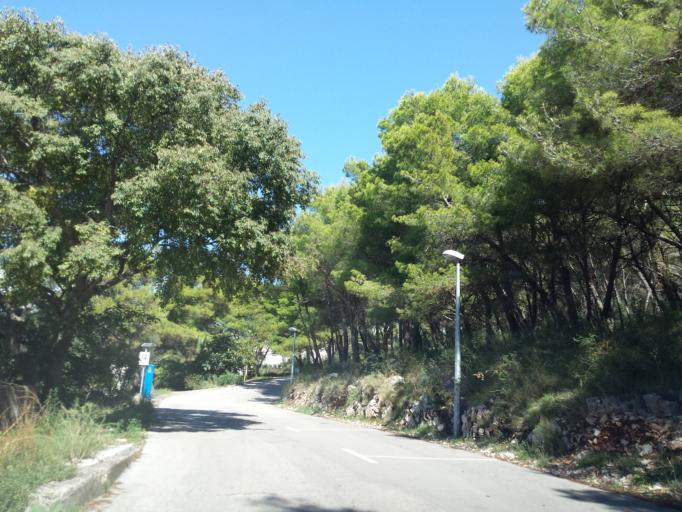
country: HR
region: Sibensko-Kniniska
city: Rogoznica
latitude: 43.5237
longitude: 15.9689
